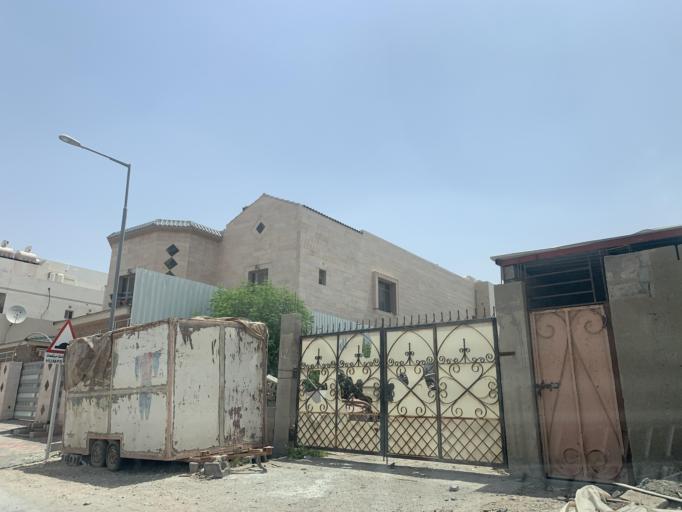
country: BH
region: Central Governorate
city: Madinat Hamad
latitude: 26.1441
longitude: 50.5052
